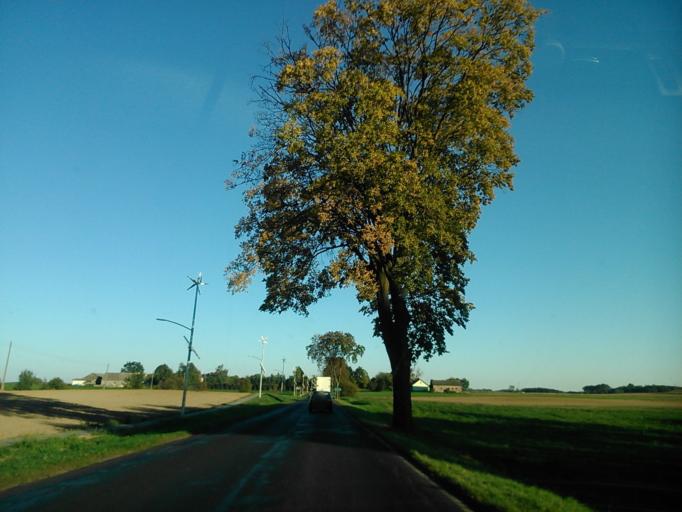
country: PL
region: Kujawsko-Pomorskie
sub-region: Powiat golubsko-dobrzynski
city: Kowalewo Pomorskie
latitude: 53.1577
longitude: 18.9316
